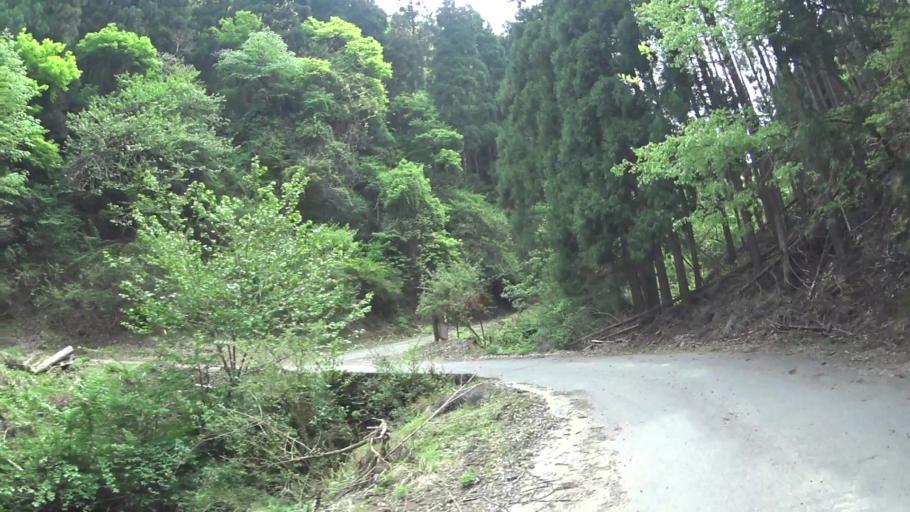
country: JP
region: Kyoto
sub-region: Kyoto-shi
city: Kamigyo-ku
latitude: 35.1801
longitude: 135.7031
